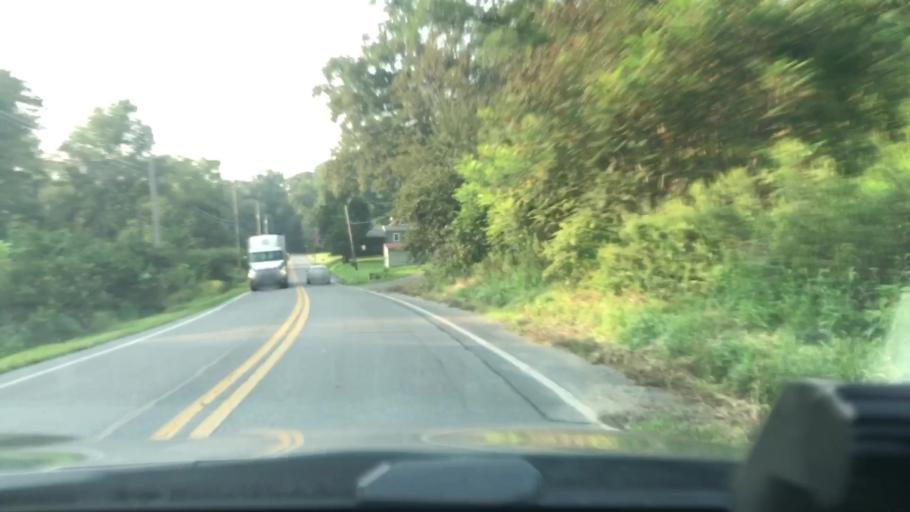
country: US
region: Pennsylvania
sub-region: Berks County
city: Kutztown
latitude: 40.5609
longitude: -75.8084
